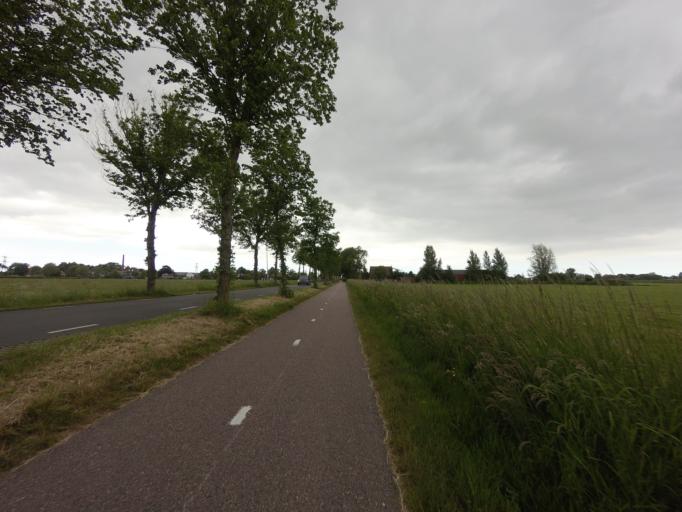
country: NL
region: North Holland
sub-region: Gemeente Hoorn
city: Hoorn
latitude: 52.6504
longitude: 5.0038
